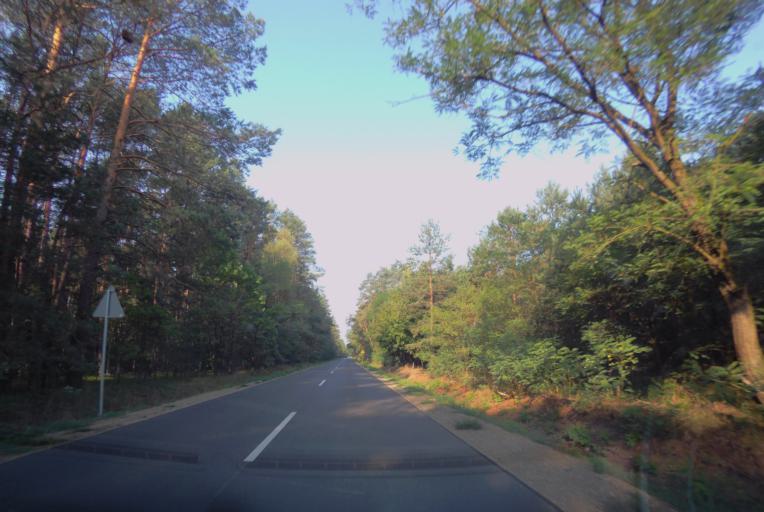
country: PL
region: Subcarpathian Voivodeship
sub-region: Powiat nizanski
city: Jarocin
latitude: 50.5100
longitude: 22.3279
